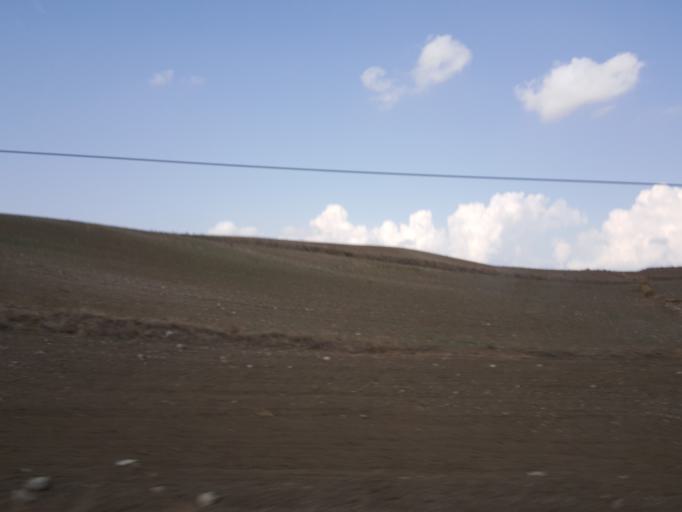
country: TR
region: Corum
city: Bogazkale
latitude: 40.1363
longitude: 34.5593
